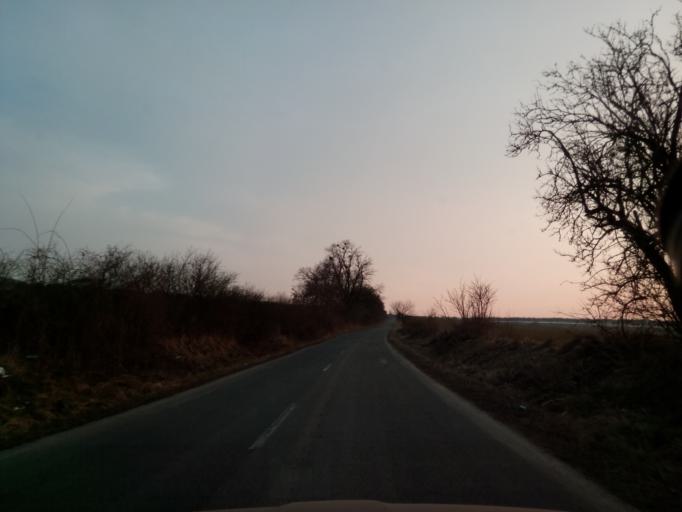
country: HU
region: Borsod-Abauj-Zemplen
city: Gonc
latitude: 48.4968
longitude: 21.3013
